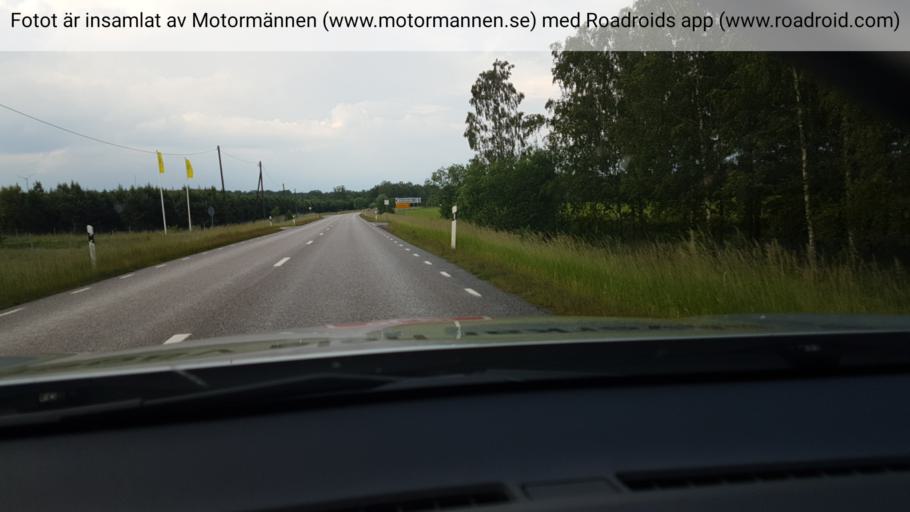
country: SE
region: Vaestra Goetaland
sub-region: Hjo Kommun
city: Hjo
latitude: 58.2478
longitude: 14.2318
